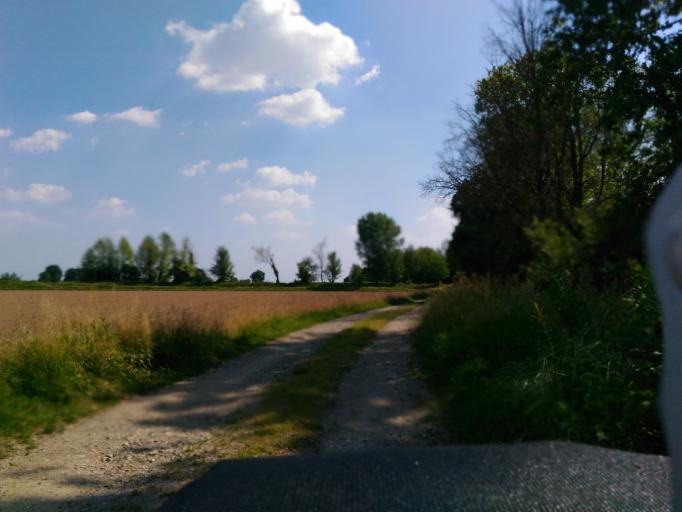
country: IT
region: Lombardy
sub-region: Citta metropolitana di Milano
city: Dresano
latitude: 45.3837
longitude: 9.3630
